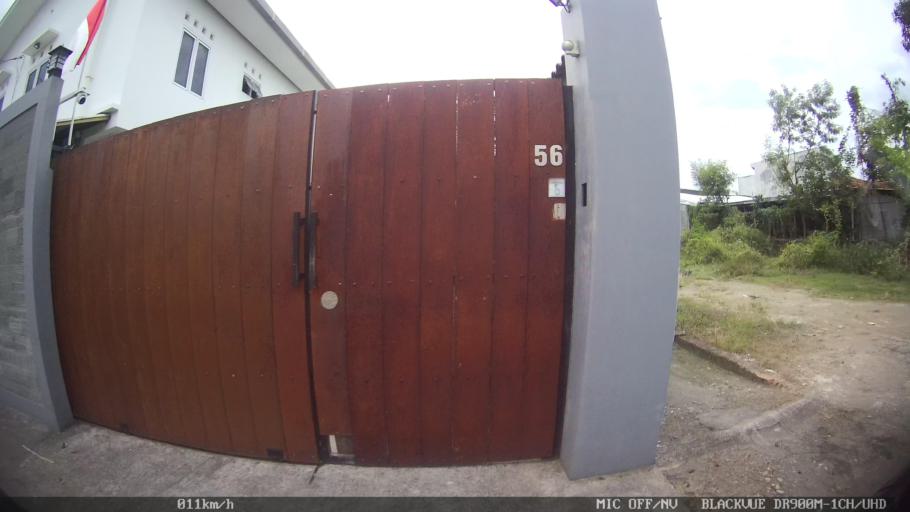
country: ID
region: Daerah Istimewa Yogyakarta
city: Depok
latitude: -7.8135
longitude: 110.4191
